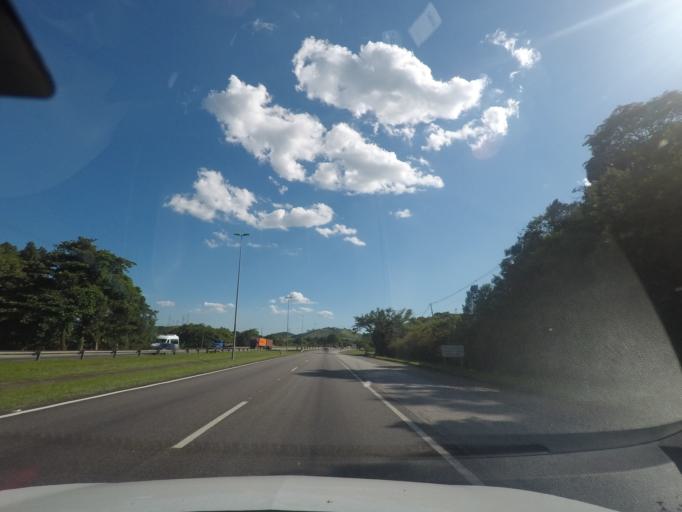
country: BR
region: Rio de Janeiro
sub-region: Guapimirim
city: Guapimirim
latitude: -22.6001
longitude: -43.0248
